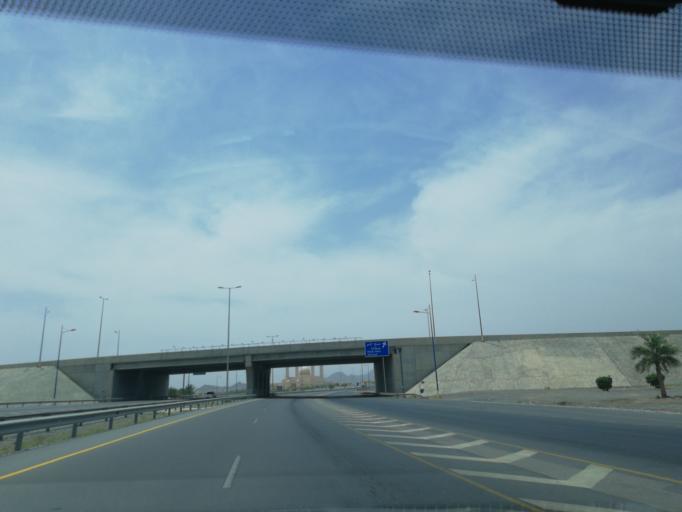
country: OM
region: Muhafazat ad Dakhiliyah
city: Nizwa
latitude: 22.8594
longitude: 57.5406
